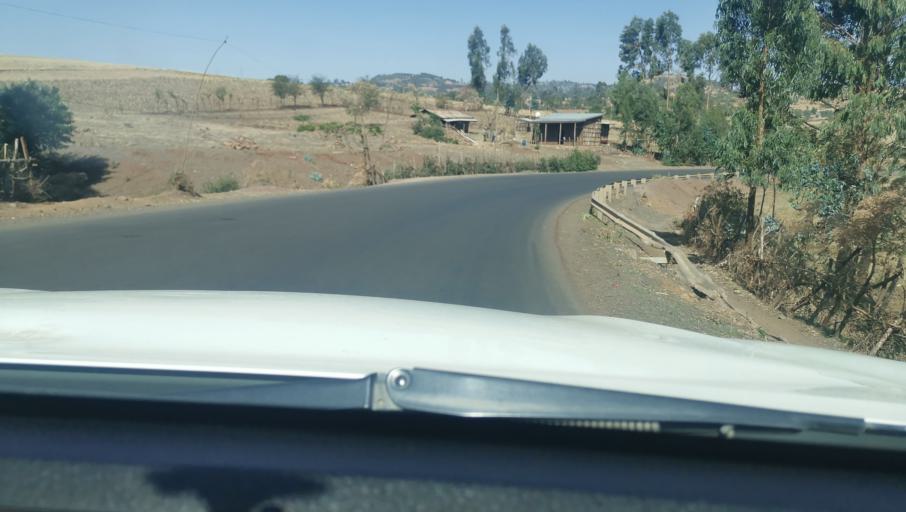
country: ET
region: Oromiya
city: Gedo
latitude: 8.9681
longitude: 37.5196
